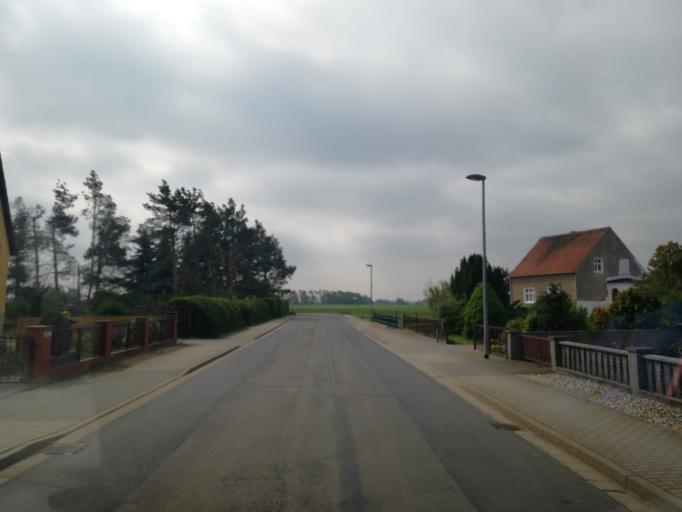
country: DE
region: Saxony
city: Beilrode
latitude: 51.6342
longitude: 13.1204
